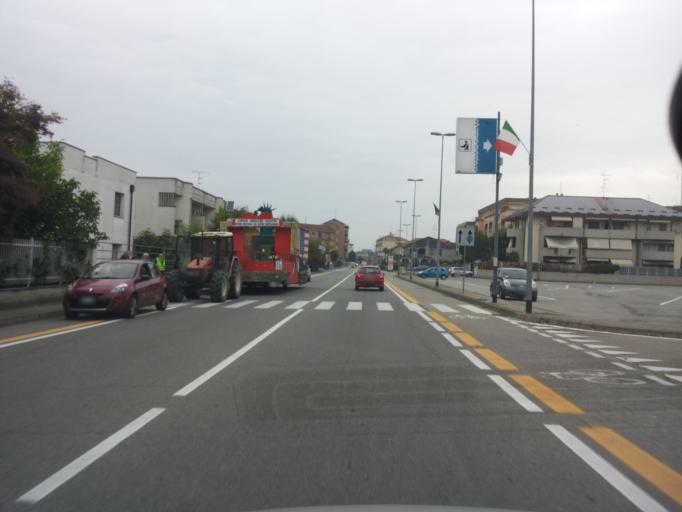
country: IT
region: Piedmont
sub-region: Provincia di Vercelli
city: Vercelli
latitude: 45.3225
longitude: 8.4351
